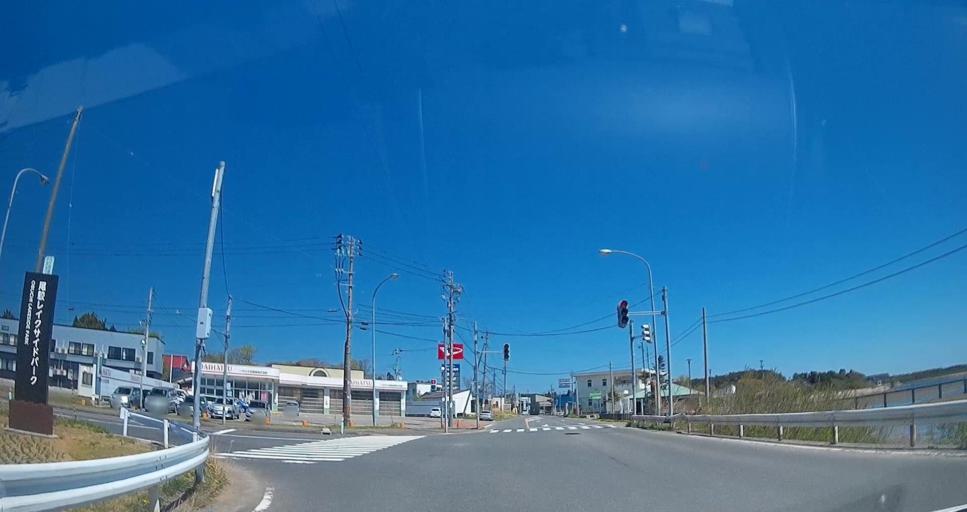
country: JP
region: Aomori
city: Misawa
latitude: 40.9599
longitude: 141.3725
